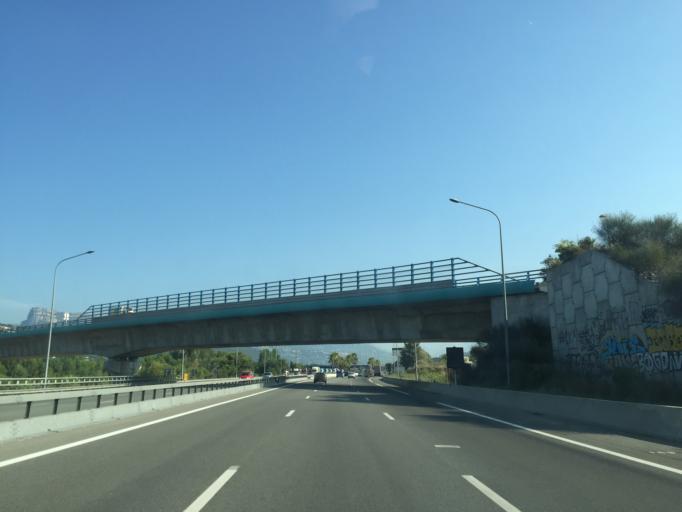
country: FR
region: Provence-Alpes-Cote d'Azur
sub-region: Departement des Alpes-Maritimes
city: Saint-Laurent-du-Var
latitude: 43.6957
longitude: 7.1891
